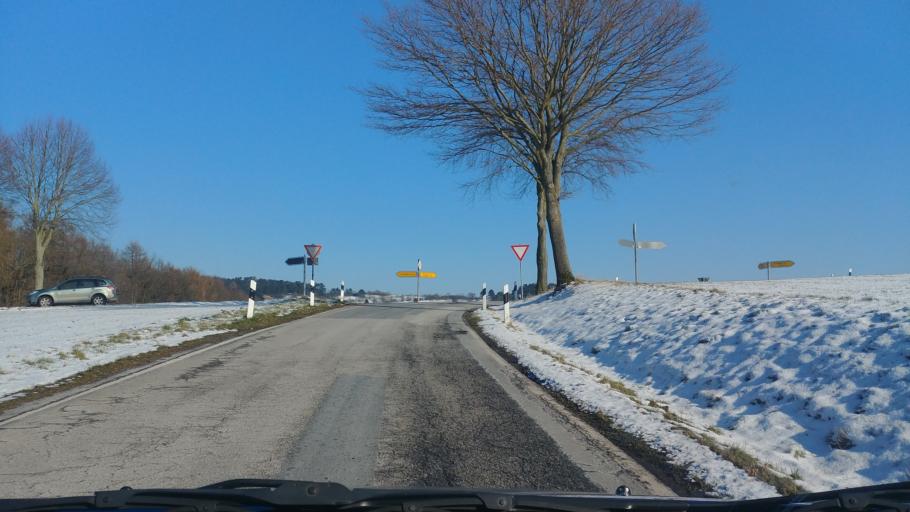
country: DE
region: Lower Saxony
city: Hardegsen
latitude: 51.7097
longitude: 9.7830
